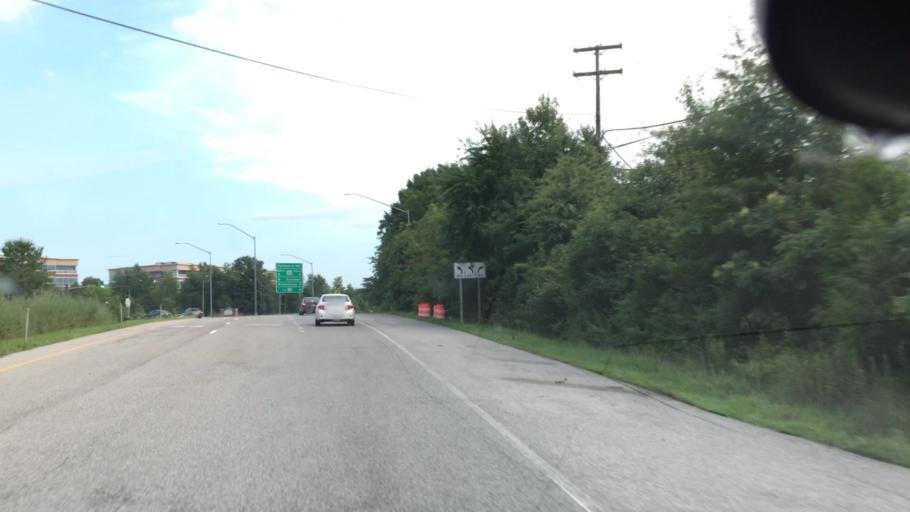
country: US
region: Maryland
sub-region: Prince George's County
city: Berwyn Heights
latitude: 39.0023
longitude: -76.8975
